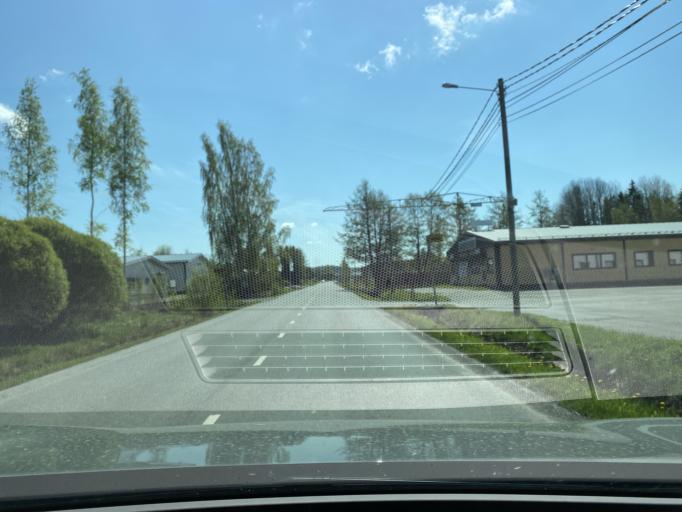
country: FI
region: Pirkanmaa
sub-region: Lounais-Pirkanmaa
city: Vammala
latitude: 61.3290
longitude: 22.9114
